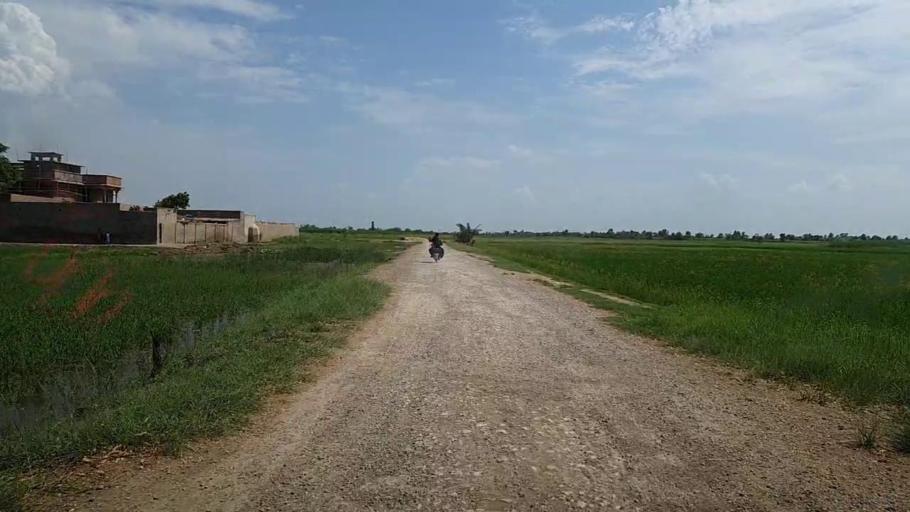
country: PK
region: Sindh
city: Bhiria
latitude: 26.9468
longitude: 68.2432
